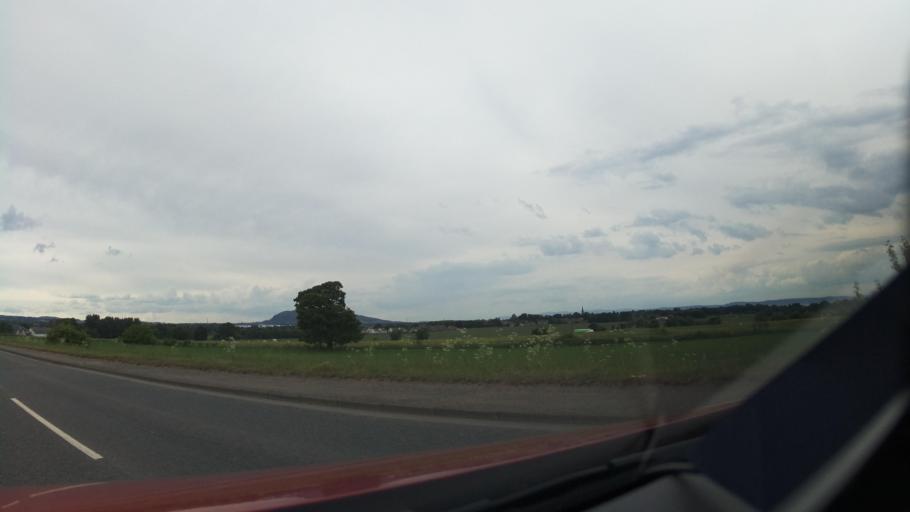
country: GB
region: Scotland
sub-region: East Lothian
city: Musselburgh
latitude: 55.9264
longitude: -3.0240
